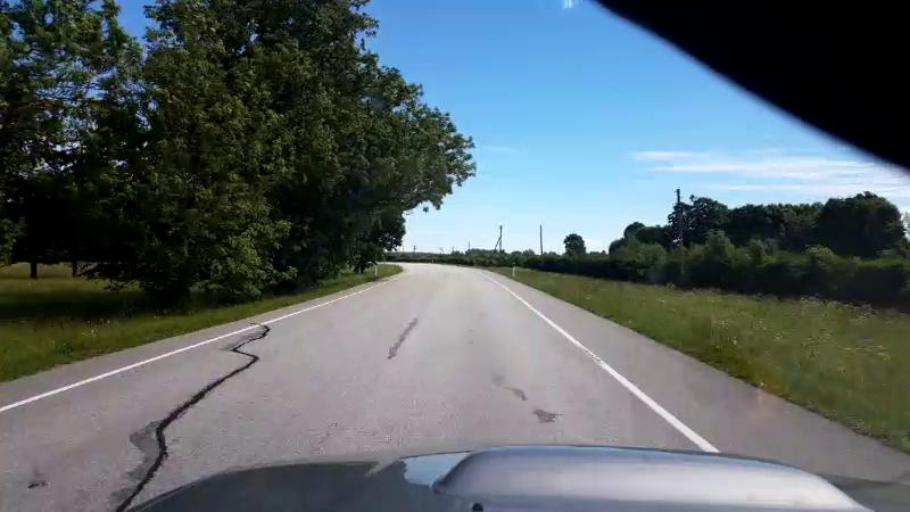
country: EE
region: Jaervamaa
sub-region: Koeru vald
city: Koeru
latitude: 58.9894
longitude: 25.9722
